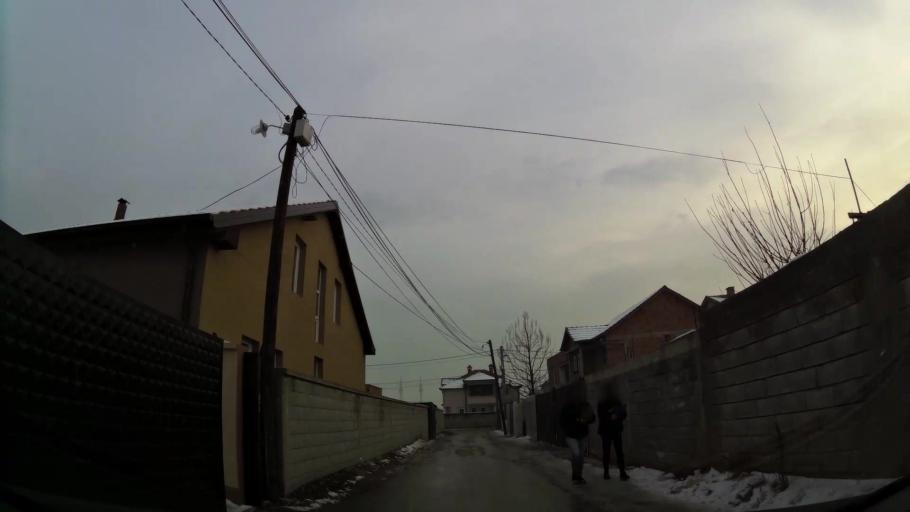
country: MK
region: Suto Orizari
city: Suto Orizare
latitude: 42.0354
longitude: 21.4163
